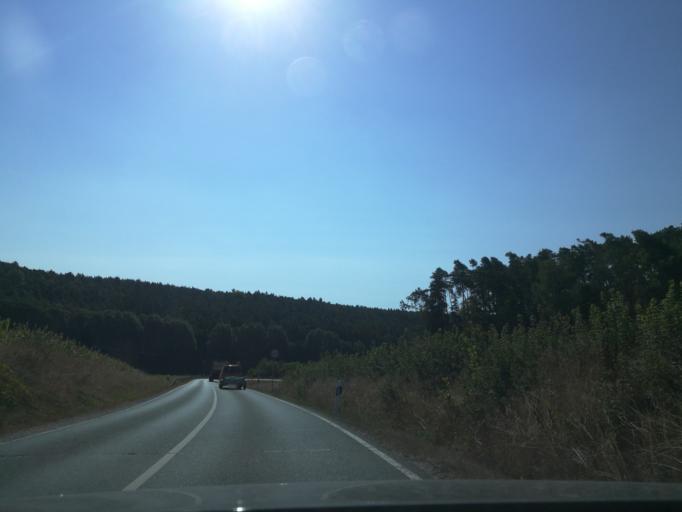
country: DE
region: Bavaria
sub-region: Regierungsbezirk Mittelfranken
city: Ammerndorf
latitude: 49.4367
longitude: 10.8529
